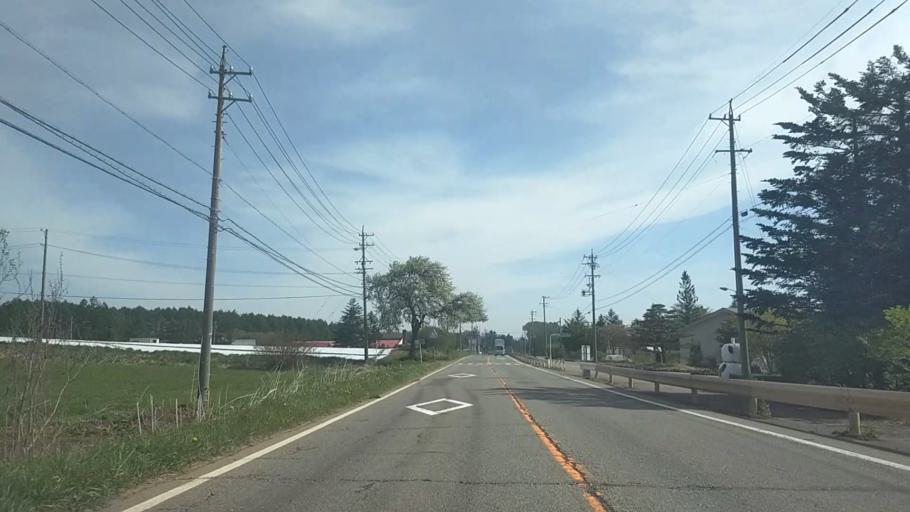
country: JP
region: Nagano
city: Saku
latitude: 35.9677
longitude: 138.4774
